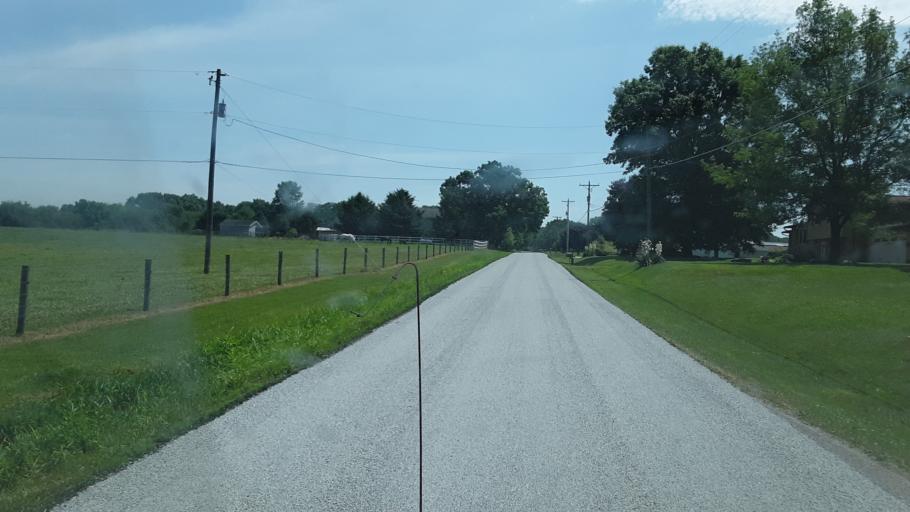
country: US
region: Ohio
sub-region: Wayne County
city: Shreve
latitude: 40.7191
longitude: -81.9570
